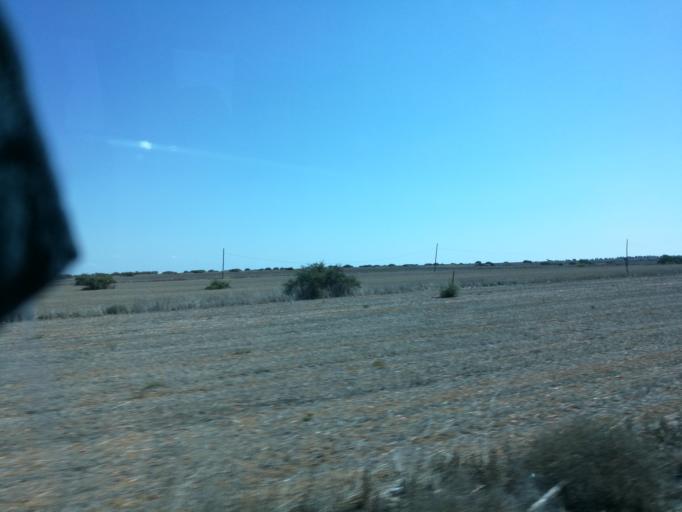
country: CY
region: Ammochostos
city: Avgorou
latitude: 35.0694
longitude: 33.8288
